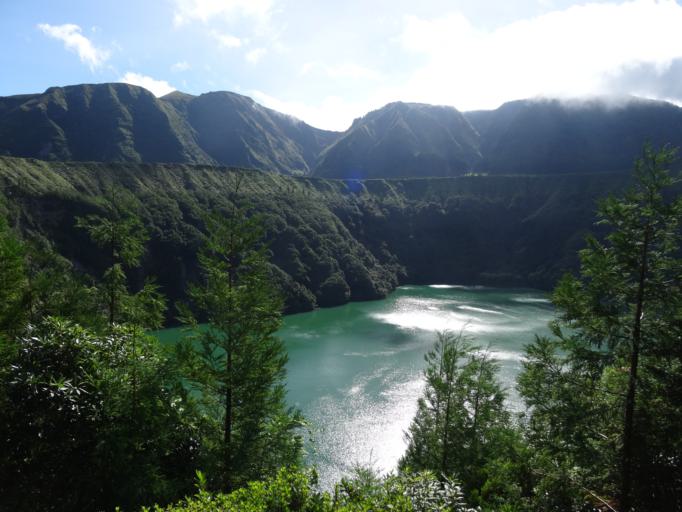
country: PT
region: Azores
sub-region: Ponta Delgada
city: Arrifes
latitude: 37.8515
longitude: -25.7774
